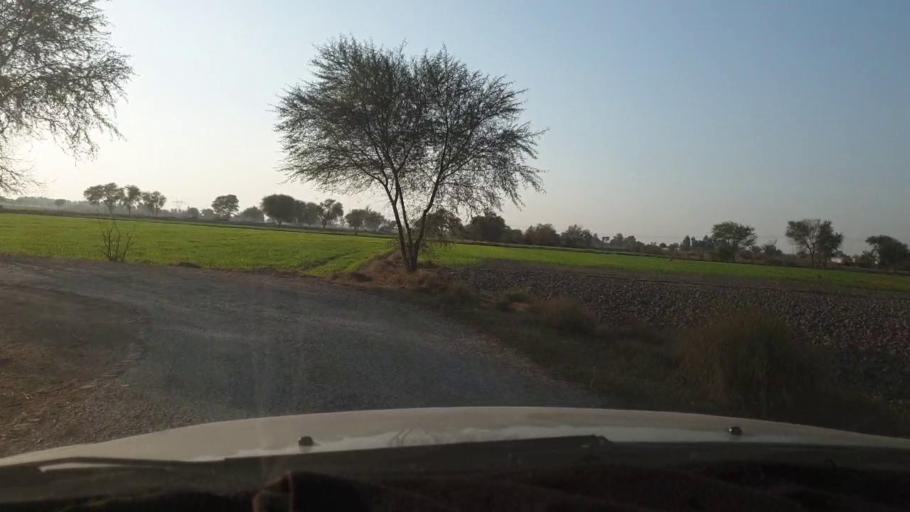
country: PK
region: Sindh
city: Mirpur Mathelo
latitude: 28.0008
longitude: 69.5060
